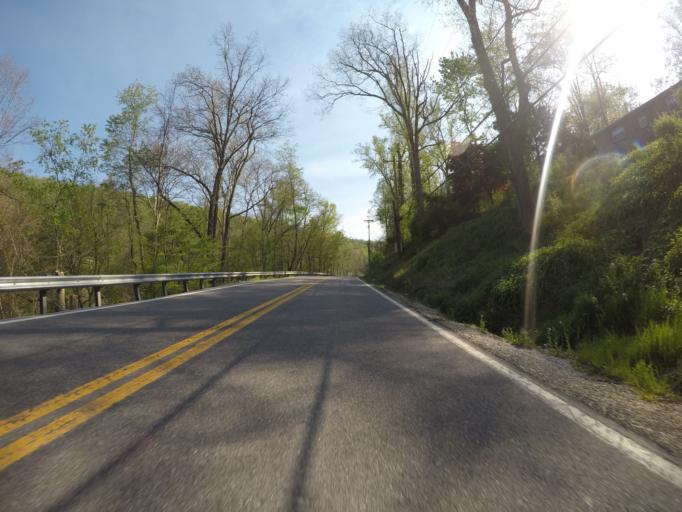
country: US
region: West Virginia
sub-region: Kanawha County
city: Coal Fork
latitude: 38.3832
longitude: -81.5609
